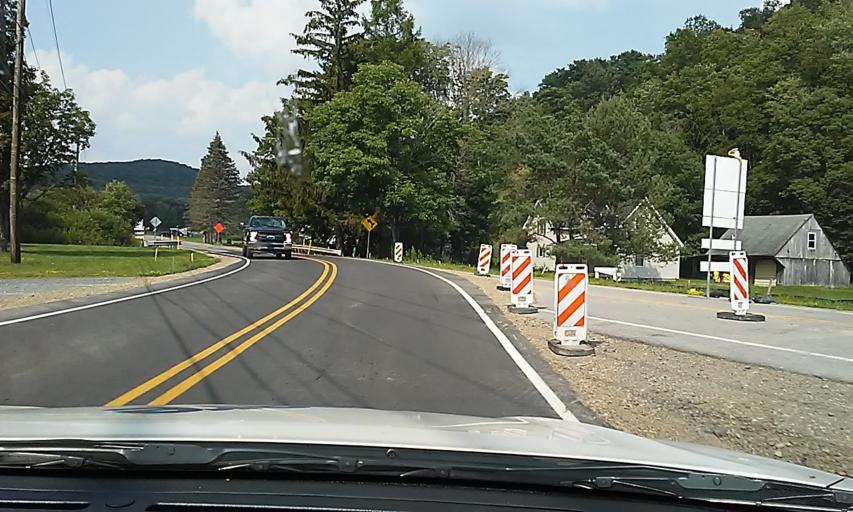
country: US
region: Pennsylvania
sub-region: Potter County
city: Galeton
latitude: 41.8298
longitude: -77.7977
